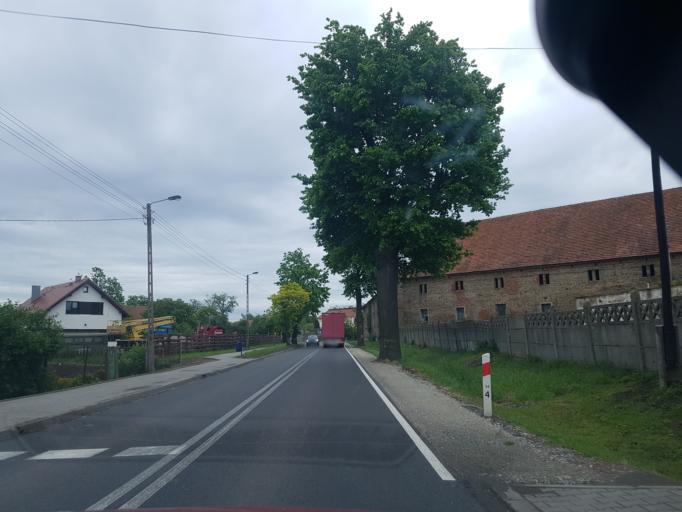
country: PL
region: Lower Silesian Voivodeship
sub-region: Powiat wroclawski
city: Kobierzyce
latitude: 50.9563
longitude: 16.8899
